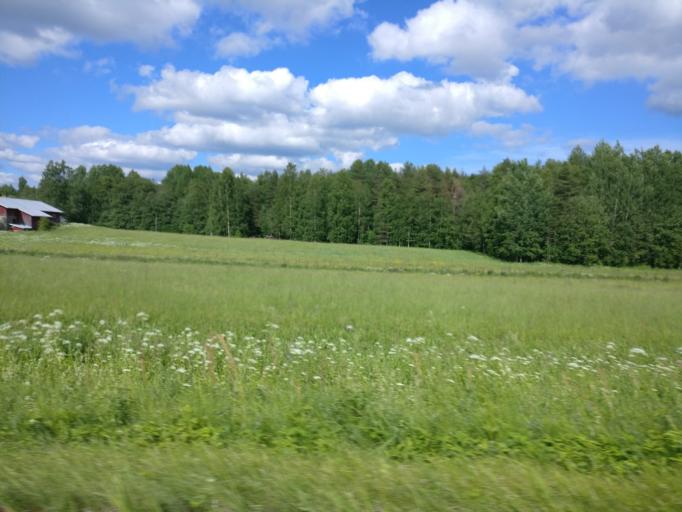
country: FI
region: Southern Savonia
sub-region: Savonlinna
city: Kerimaeki
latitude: 61.8663
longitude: 29.1360
